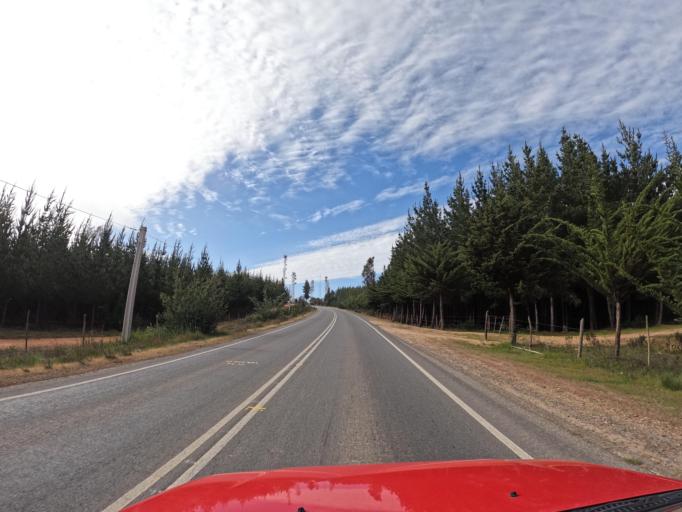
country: CL
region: O'Higgins
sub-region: Provincia de Colchagua
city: Santa Cruz
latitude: -34.3375
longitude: -71.8751
